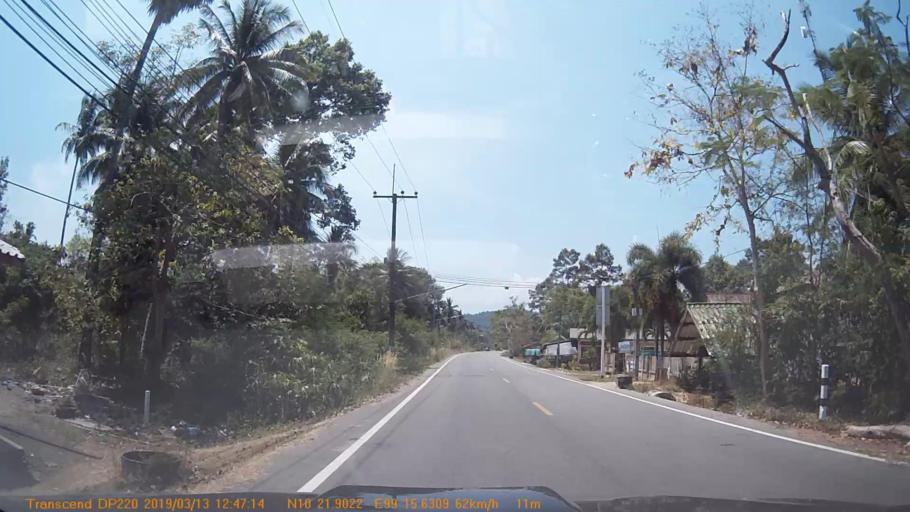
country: TH
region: Chumphon
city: Chumphon
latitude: 10.3650
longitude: 99.2601
